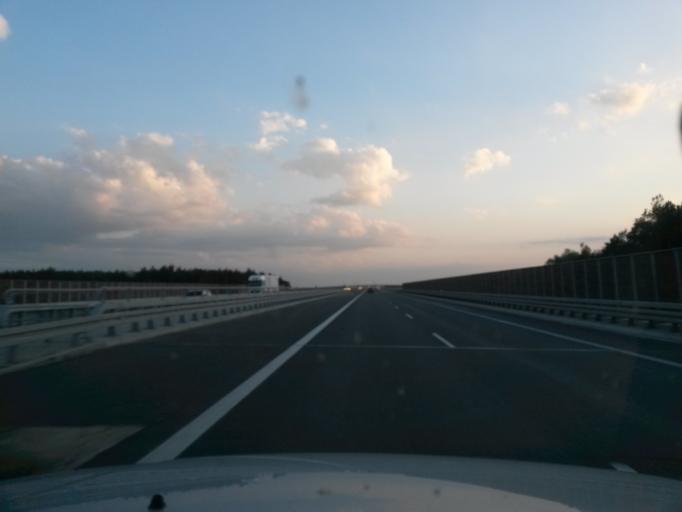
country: PL
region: Lodz Voivodeship
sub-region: Powiat wieruszowski
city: Wieruszow
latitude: 51.3308
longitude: 18.0889
